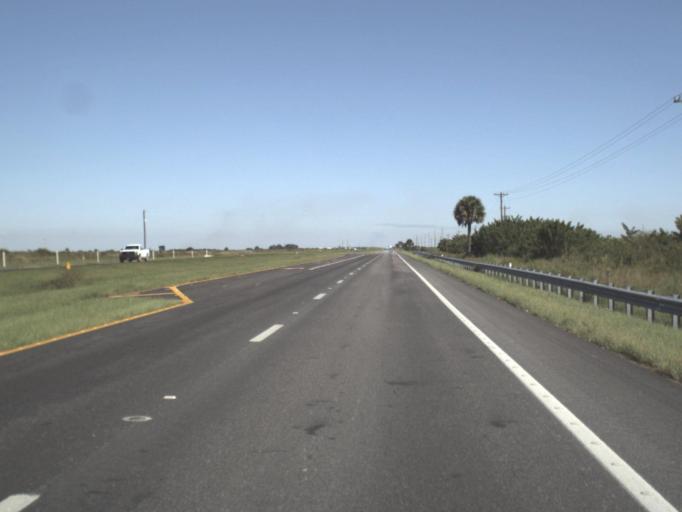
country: US
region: Florida
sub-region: Glades County
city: Moore Haven
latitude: 26.7528
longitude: -81.1232
